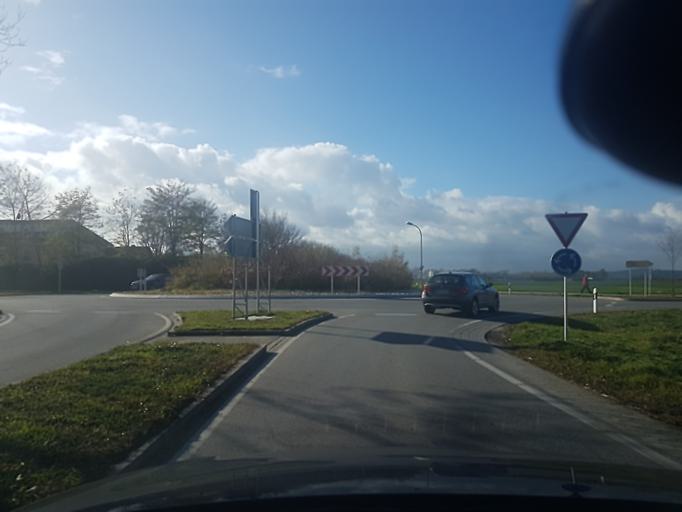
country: DE
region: Bavaria
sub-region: Lower Bavaria
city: Niederviehbach
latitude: 48.6290
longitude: 12.3792
